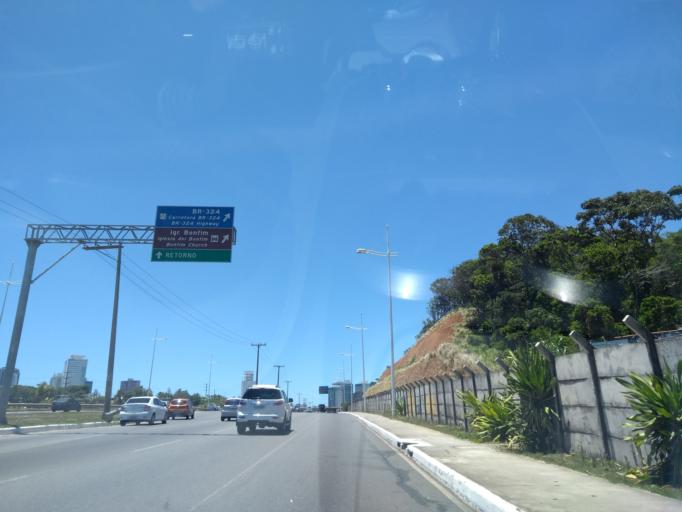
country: BR
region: Bahia
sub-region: Salvador
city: Salvador
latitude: -12.9715
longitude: -38.4467
